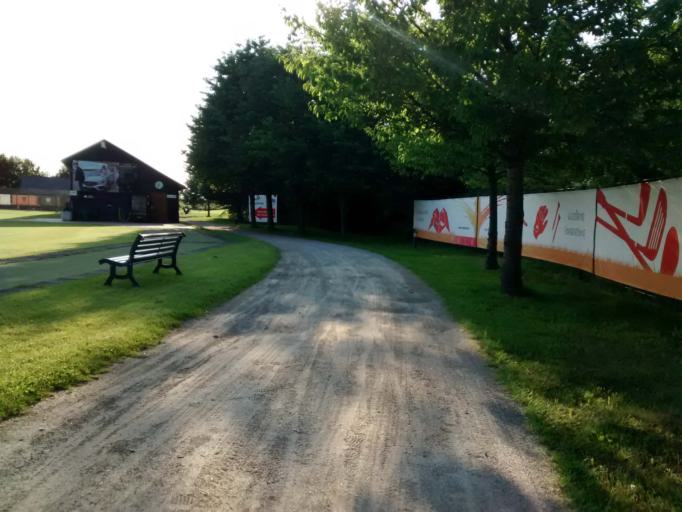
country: DE
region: Brandenburg
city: Hohen Neuendorf
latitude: 52.6524
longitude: 13.2541
